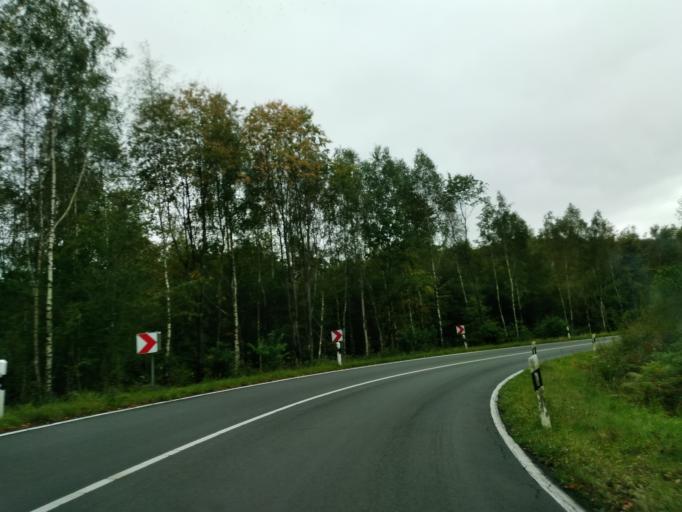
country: DE
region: North Rhine-Westphalia
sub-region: Regierungsbezirk Koln
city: Bad Honnef
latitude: 50.6735
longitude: 7.2869
